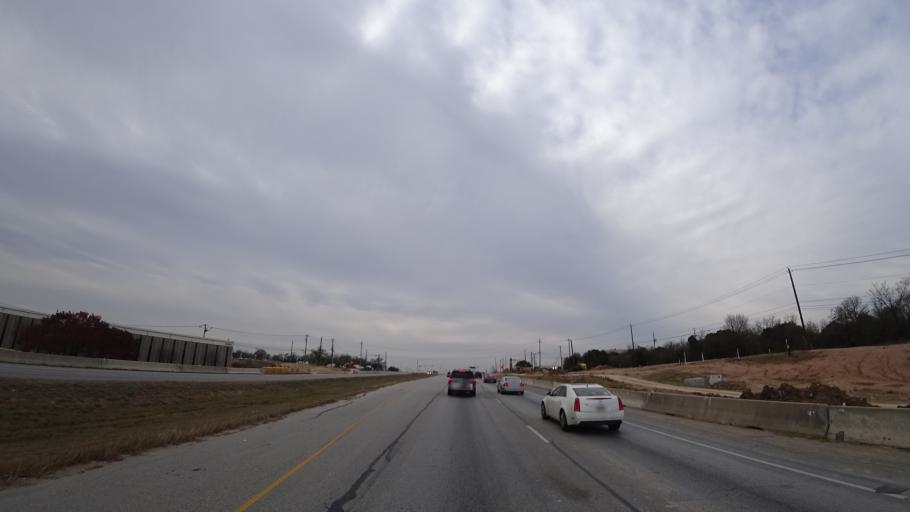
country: US
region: Texas
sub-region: Travis County
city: Austin
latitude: 30.2784
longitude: -97.6674
